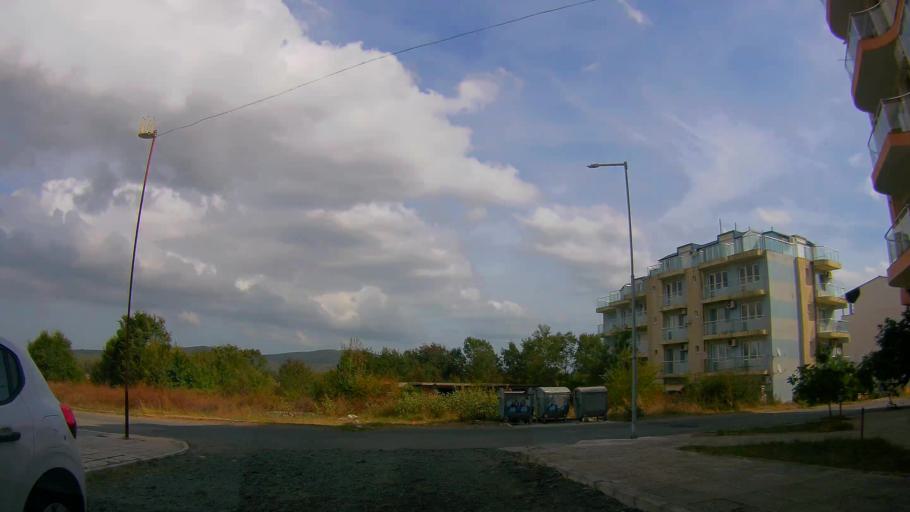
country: BG
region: Burgas
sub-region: Obshtina Primorsko
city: Primorsko
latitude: 42.2744
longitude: 27.7511
